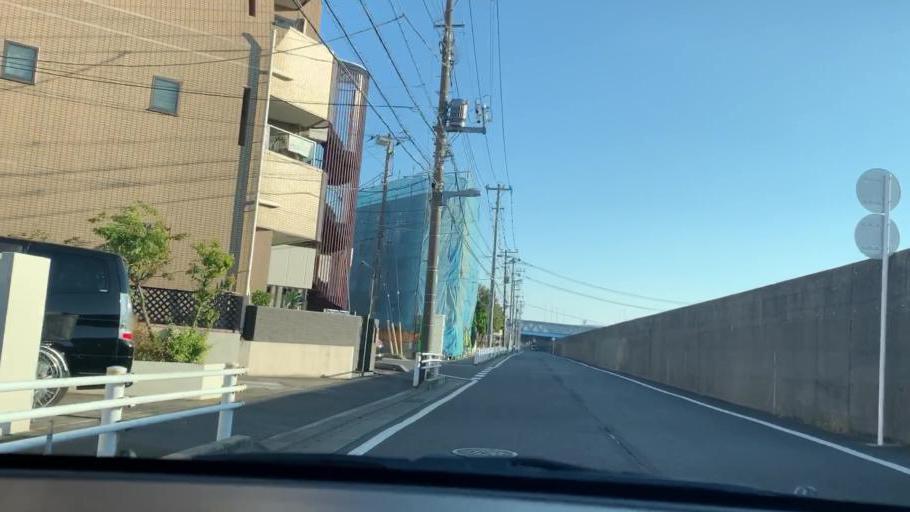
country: JP
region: Tokyo
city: Urayasu
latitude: 35.6417
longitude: 139.8869
